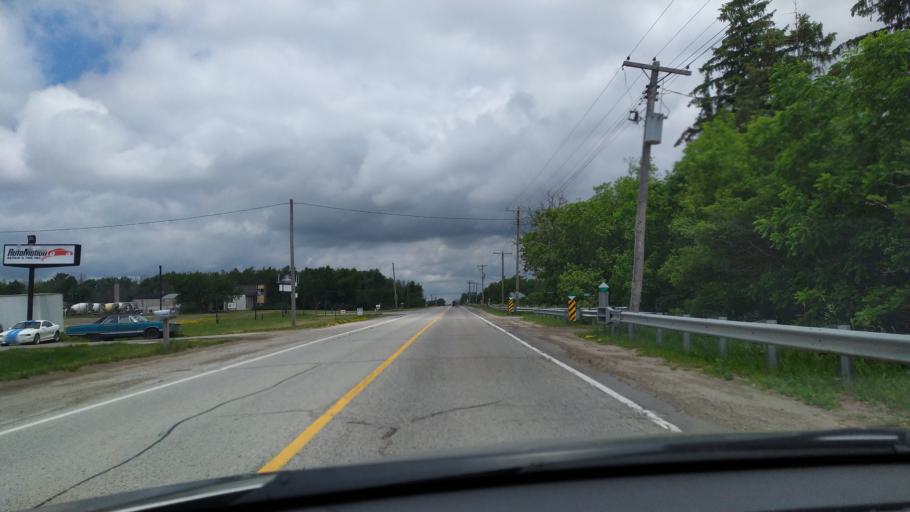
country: CA
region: Ontario
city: Stratford
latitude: 43.3915
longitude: -80.9660
